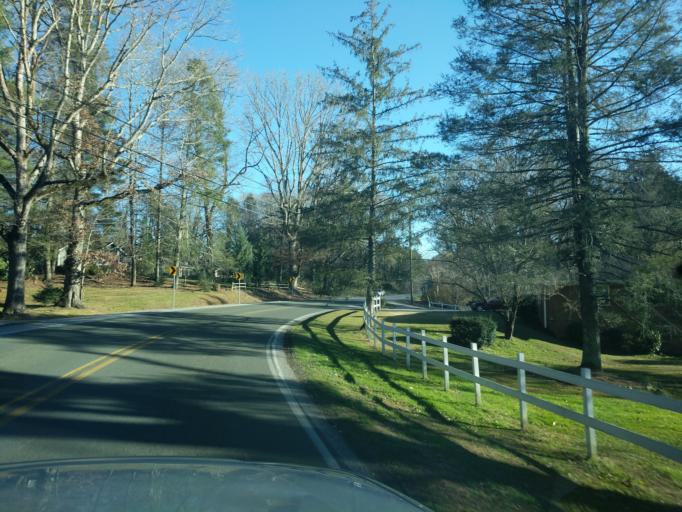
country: US
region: Georgia
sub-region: Rabun County
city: Clayton
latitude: 34.8831
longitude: -83.4127
